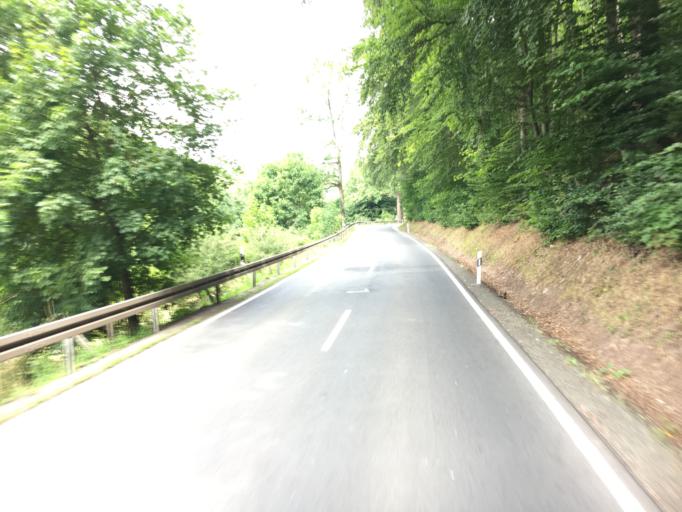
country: DE
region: Thuringia
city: Trusetal
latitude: 50.7979
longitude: 10.4280
